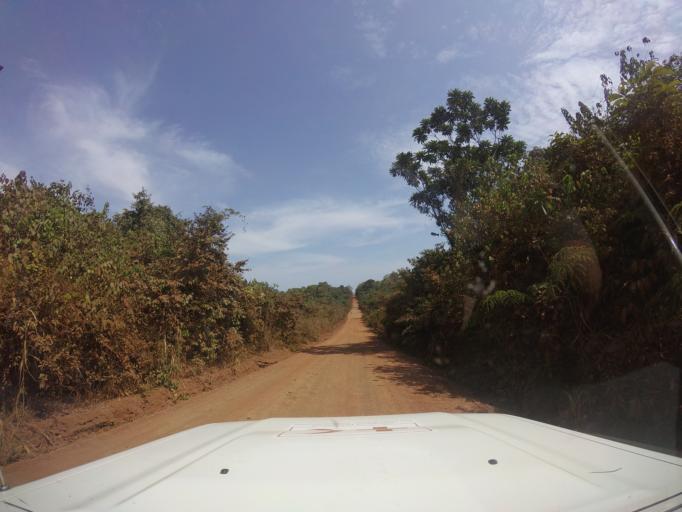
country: LR
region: Grand Cape Mount
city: Robertsport
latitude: 6.7289
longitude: -11.3394
